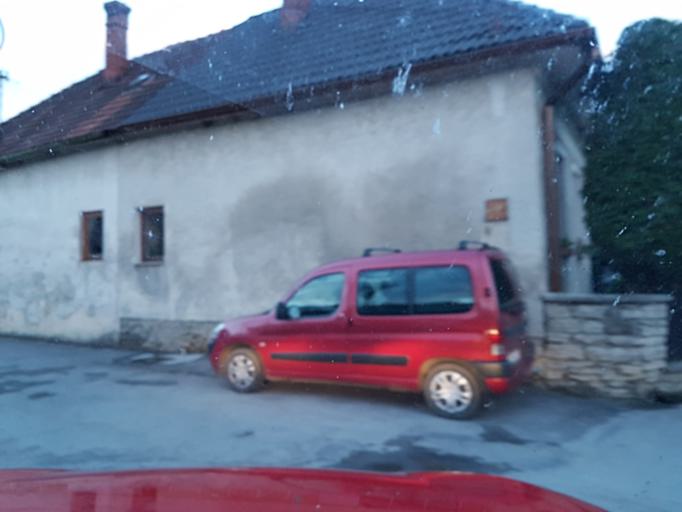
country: SK
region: Zilinsky
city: Ruzomberok
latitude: 49.1253
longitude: 19.4129
